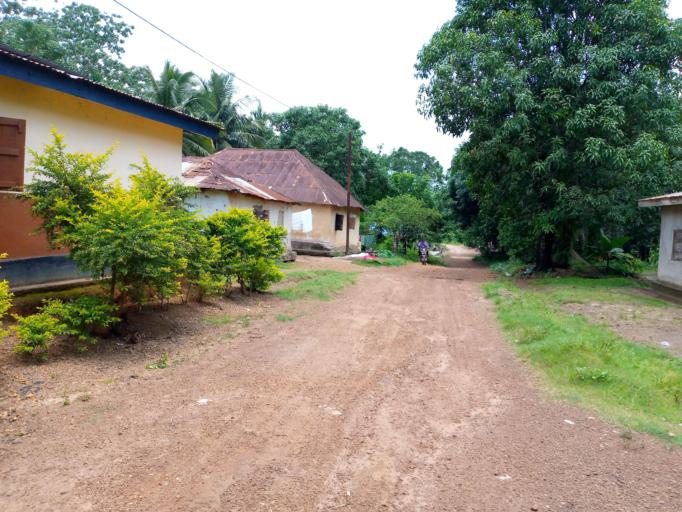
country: SL
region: Northern Province
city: Magburaka
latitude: 8.7155
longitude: -11.9517
